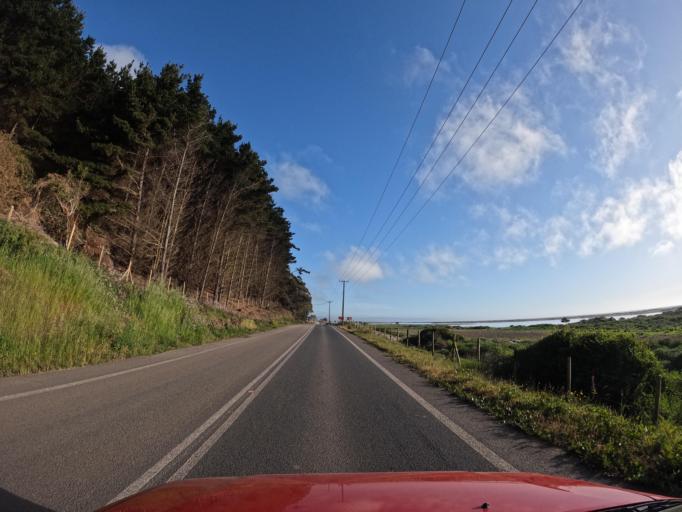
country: CL
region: Maule
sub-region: Provincia de Talca
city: Constitucion
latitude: -34.9918
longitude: -72.1787
